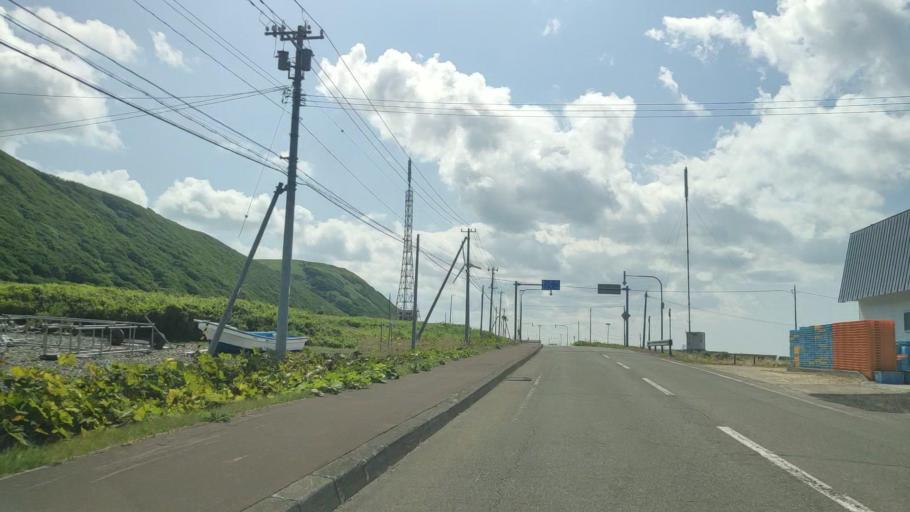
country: JP
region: Hokkaido
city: Wakkanai
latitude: 45.4096
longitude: 141.6360
